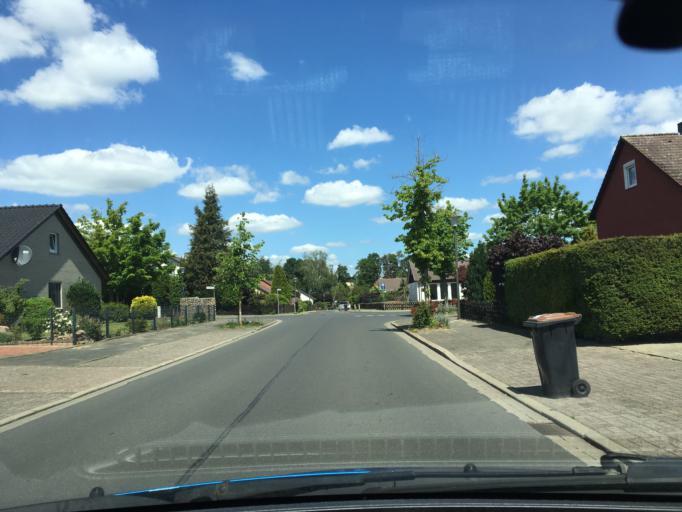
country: DE
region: Lower Saxony
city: Uelzen
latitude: 52.9677
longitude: 10.5321
